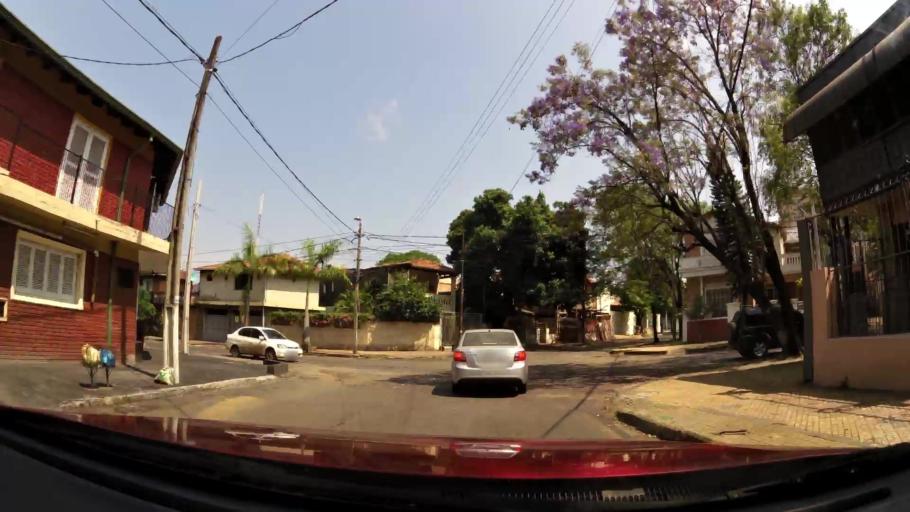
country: PY
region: Asuncion
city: Asuncion
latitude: -25.2900
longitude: -57.6516
